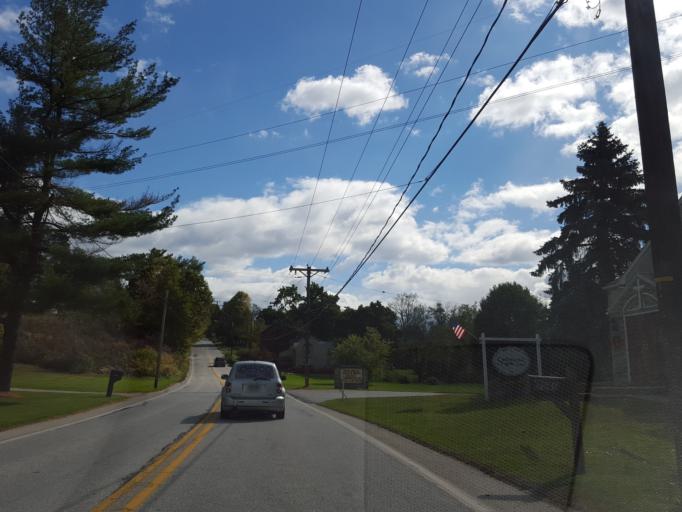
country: US
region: Pennsylvania
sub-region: York County
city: Spry
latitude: 39.9350
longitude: -76.6781
